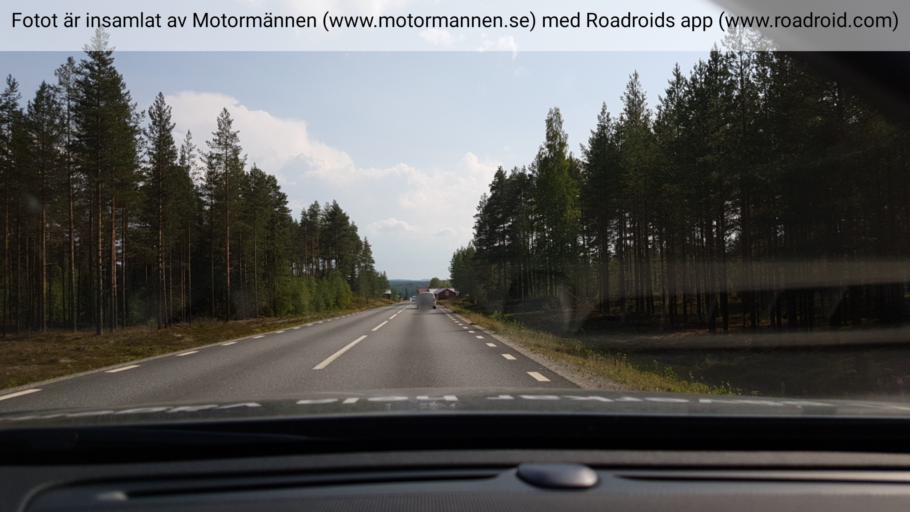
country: SE
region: Vaesterbotten
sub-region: Bjurholms Kommun
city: Bjurholm
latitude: 64.3104
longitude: 19.1626
